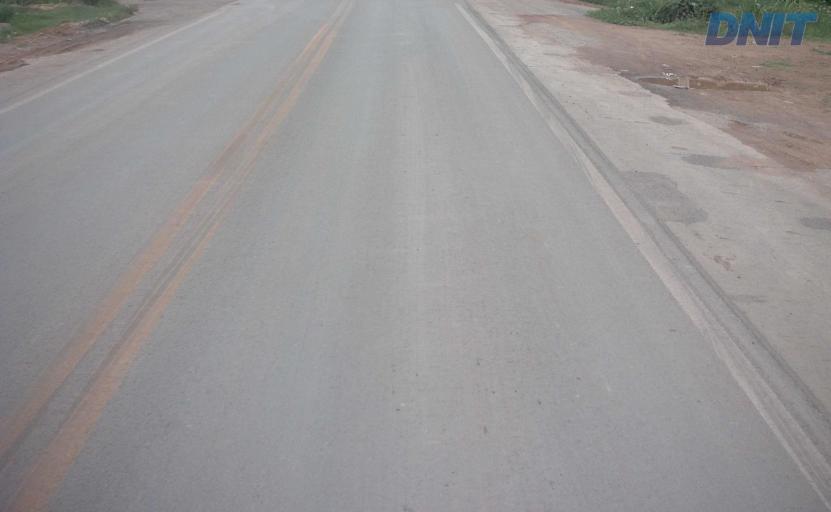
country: BR
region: Goias
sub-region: Padre Bernardo
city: Padre Bernardo
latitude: -15.1659
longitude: -48.2923
